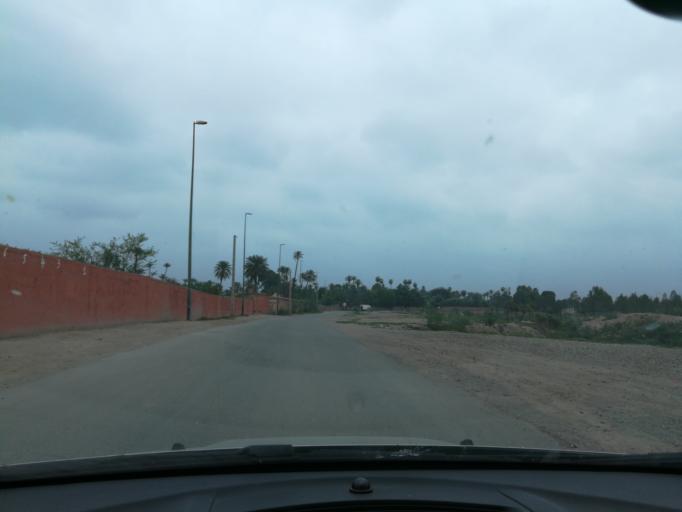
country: MA
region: Marrakech-Tensift-Al Haouz
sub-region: Marrakech
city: Marrakesh
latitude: 31.6624
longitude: -7.9838
